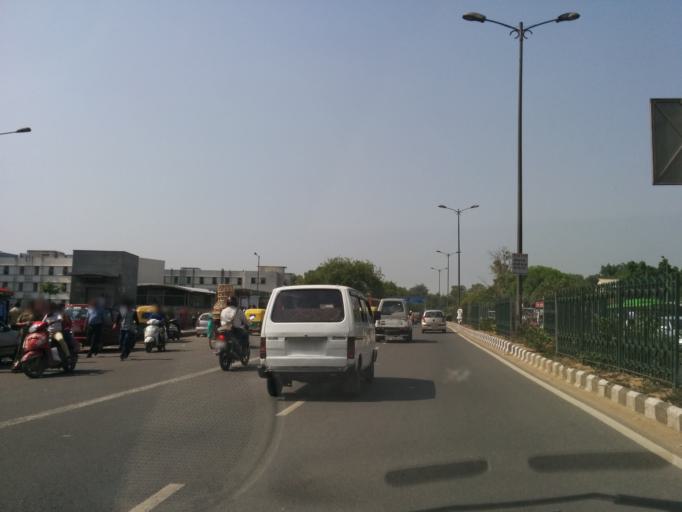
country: IN
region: NCT
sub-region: New Delhi
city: New Delhi
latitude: 28.5675
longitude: 77.2080
